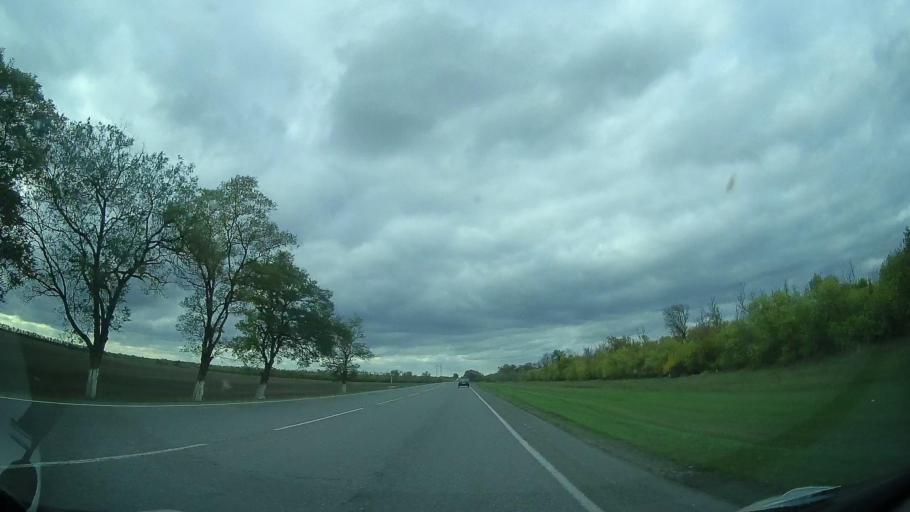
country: RU
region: Rostov
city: Zernograd
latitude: 46.8184
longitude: 40.2616
